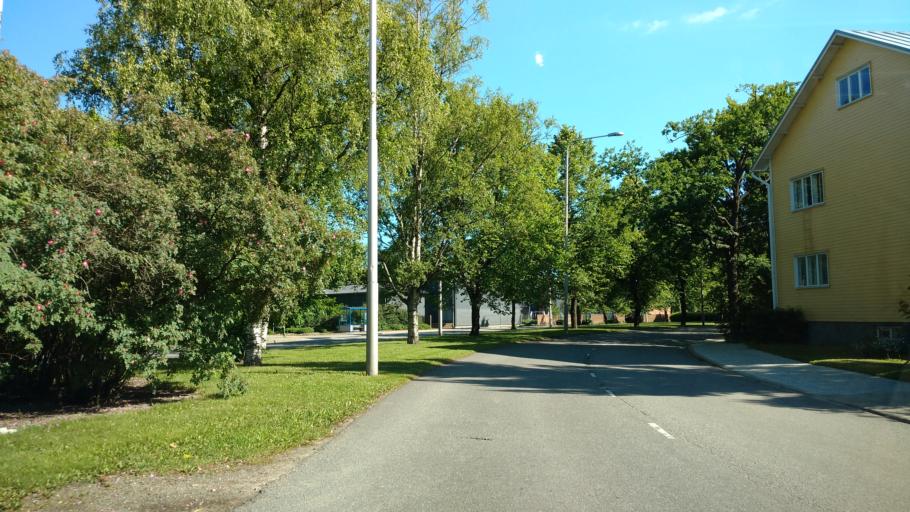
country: FI
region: Varsinais-Suomi
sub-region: Salo
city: Salo
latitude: 60.3869
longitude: 23.1386
